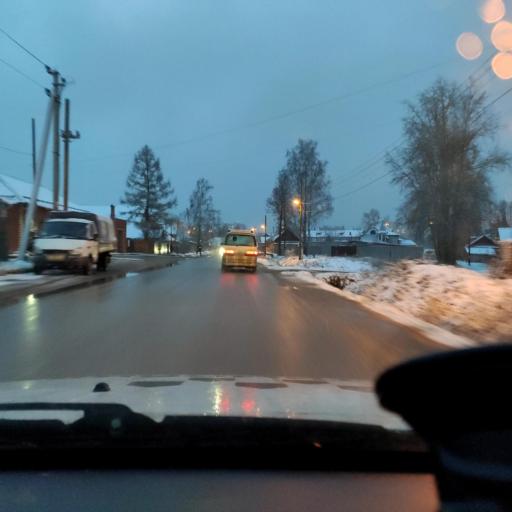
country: RU
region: Perm
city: Kondratovo
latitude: 58.0483
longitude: 56.0307
